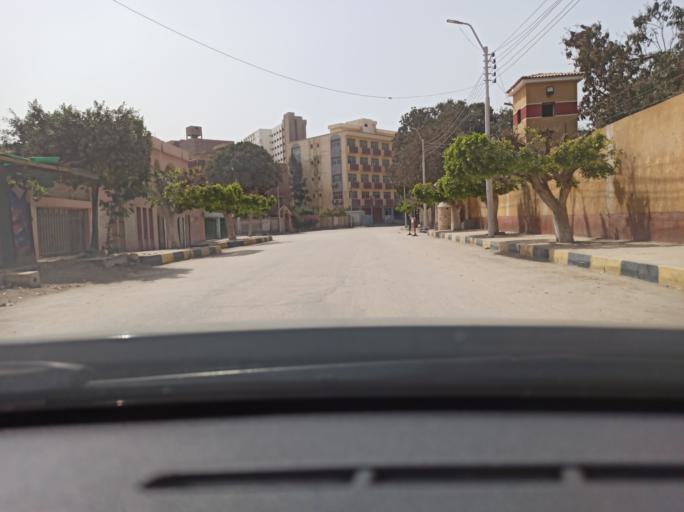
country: EG
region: Muhafazat Bani Suwayf
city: Bani Suwayf
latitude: 29.0834
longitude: 31.0932
